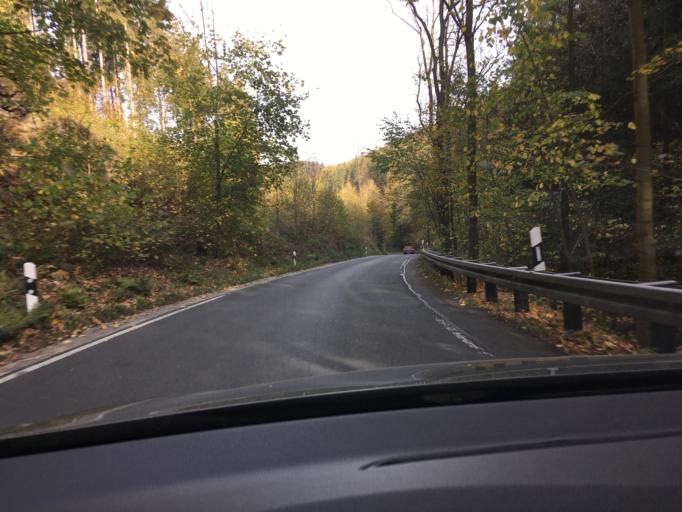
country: DE
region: Saxony
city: Glashutte
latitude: 50.8476
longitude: 13.7962
